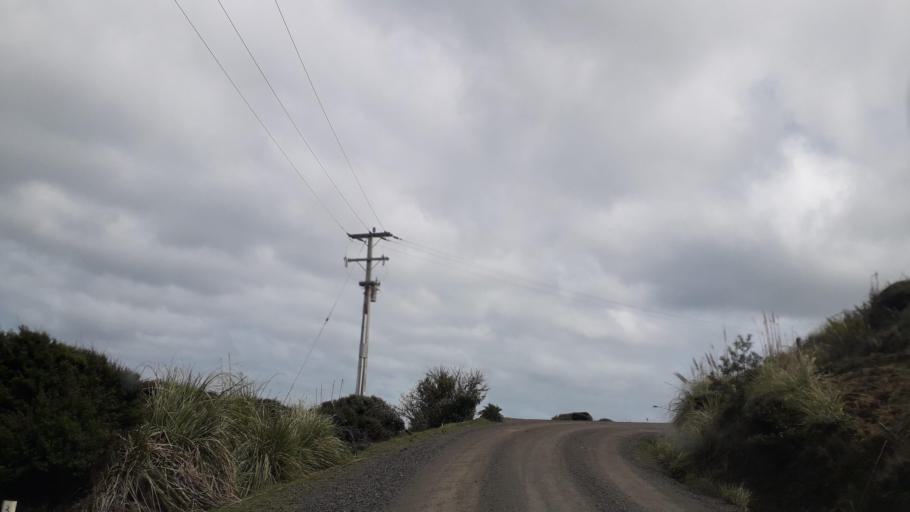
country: NZ
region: Northland
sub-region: Far North District
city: Ahipara
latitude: -35.4337
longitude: 173.2810
